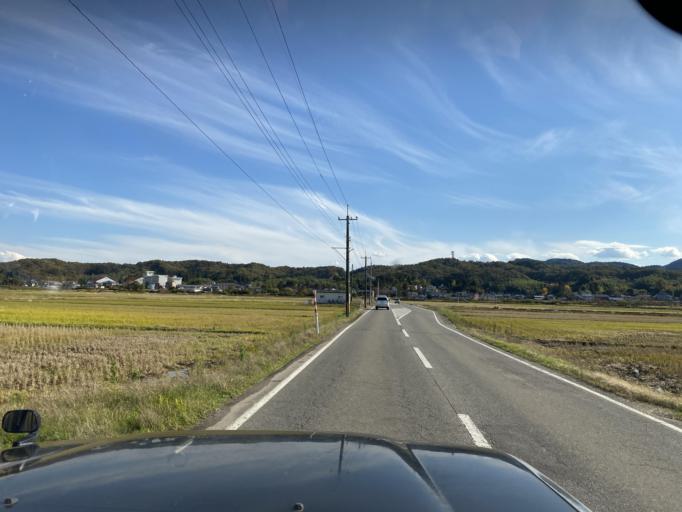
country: JP
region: Niigata
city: Niitsu-honcho
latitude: 37.7554
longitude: 139.0934
